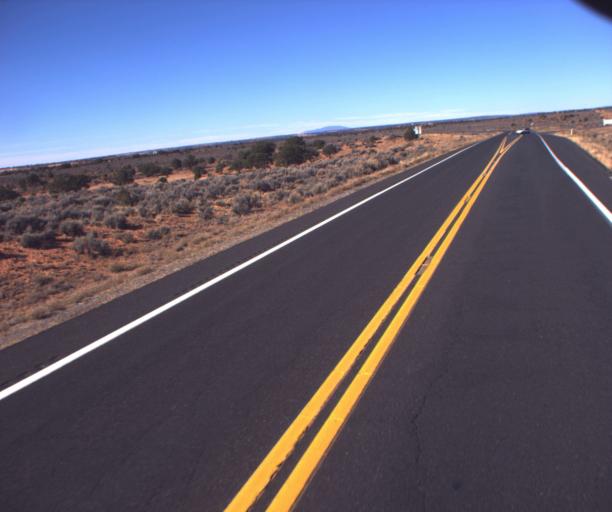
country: US
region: Arizona
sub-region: Coconino County
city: Kaibito
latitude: 36.5446
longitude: -110.7009
